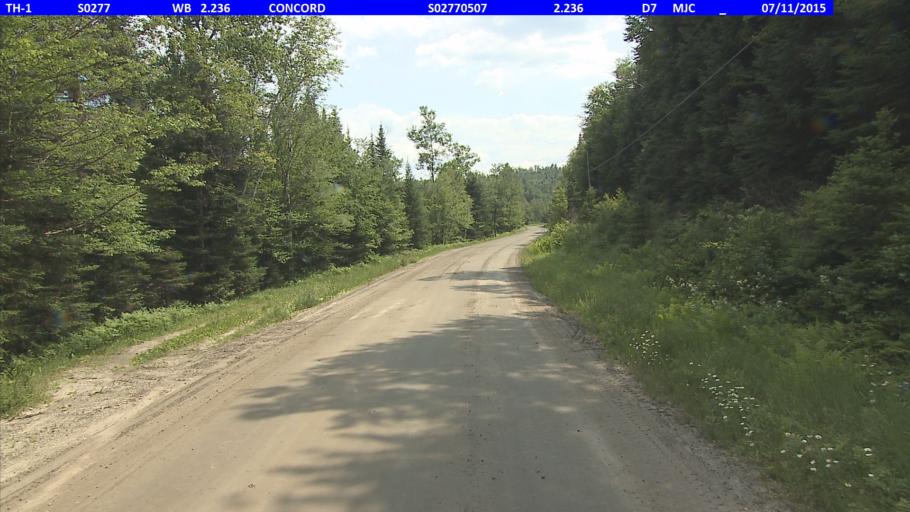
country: US
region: Vermont
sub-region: Caledonia County
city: Lyndonville
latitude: 44.4933
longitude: -71.8549
